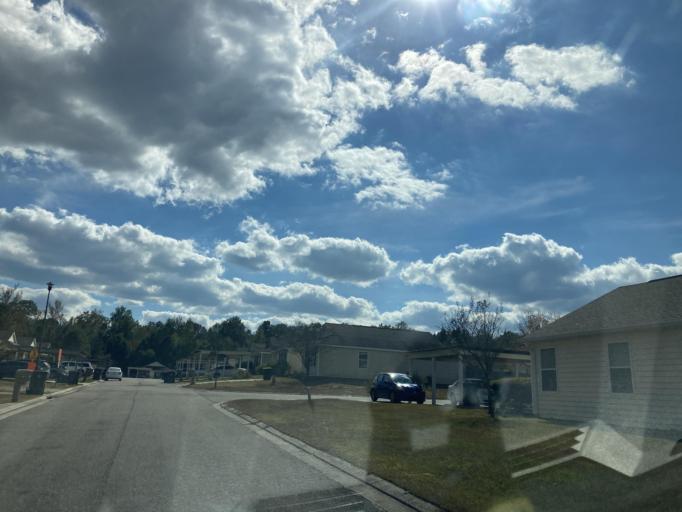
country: US
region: Mississippi
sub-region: Lamar County
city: Arnold Line
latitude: 31.3417
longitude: -89.3909
